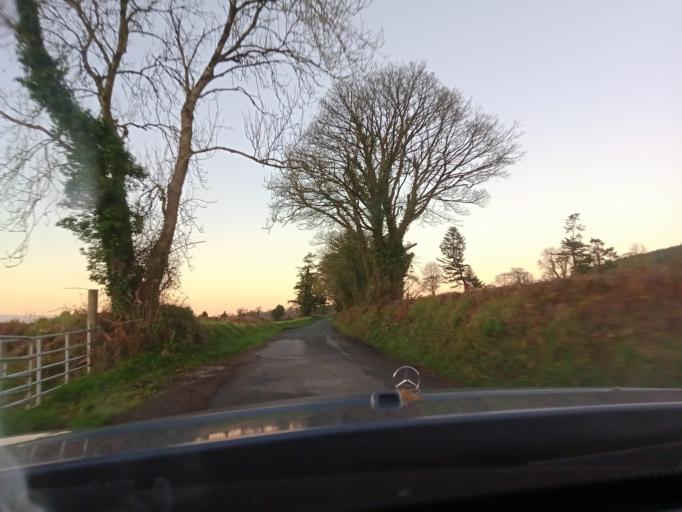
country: IE
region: Leinster
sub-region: Kilkenny
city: Thomastown
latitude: 52.4422
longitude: -7.1066
